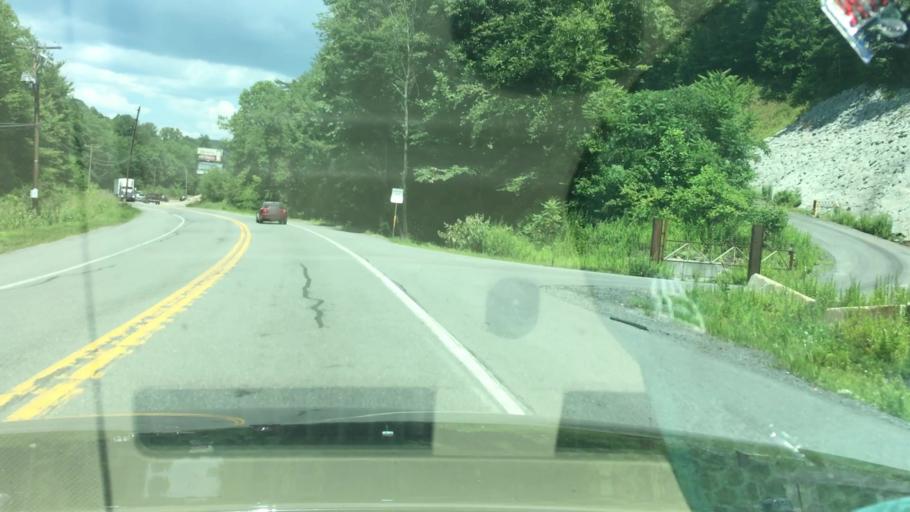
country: US
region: Pennsylvania
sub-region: Schuylkill County
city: Minersville
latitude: 40.6668
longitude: -76.2369
